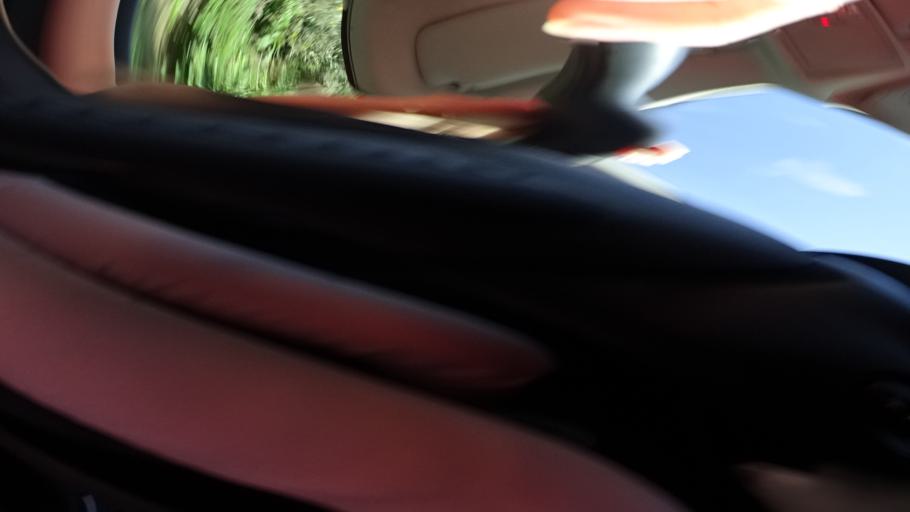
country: ES
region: Canary Islands
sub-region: Provincia de Las Palmas
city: Vega de San Mateo
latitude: 28.0254
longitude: -15.5552
